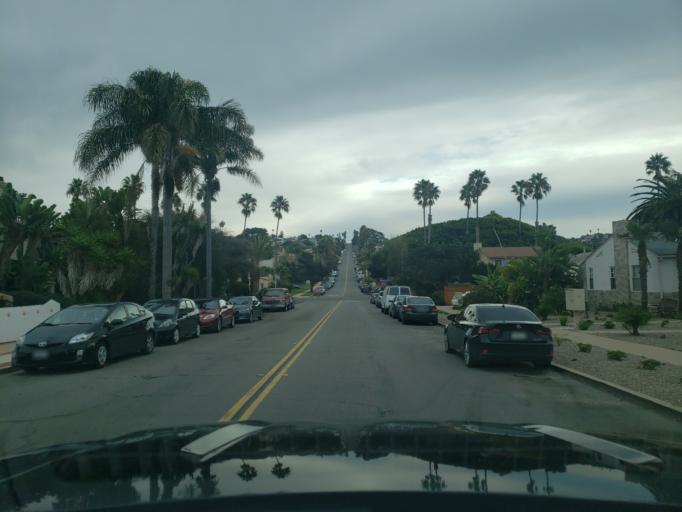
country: US
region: California
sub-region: San Diego County
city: Coronado
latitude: 32.7393
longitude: -117.2535
